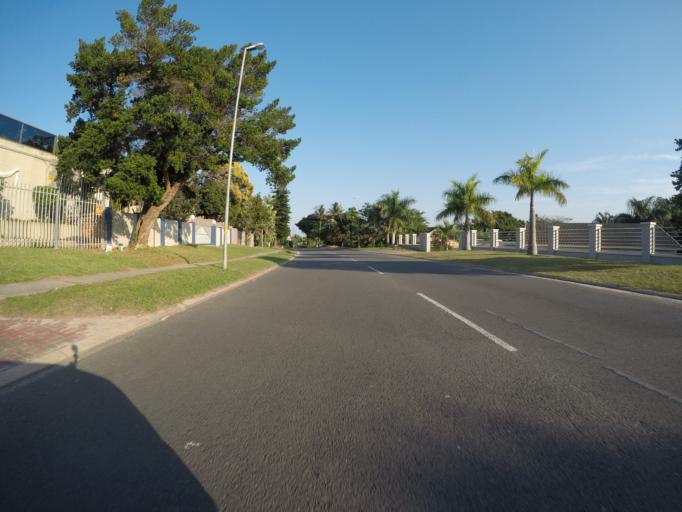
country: ZA
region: KwaZulu-Natal
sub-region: uThungulu District Municipality
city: Richards Bay
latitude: -28.7727
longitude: 32.1132
